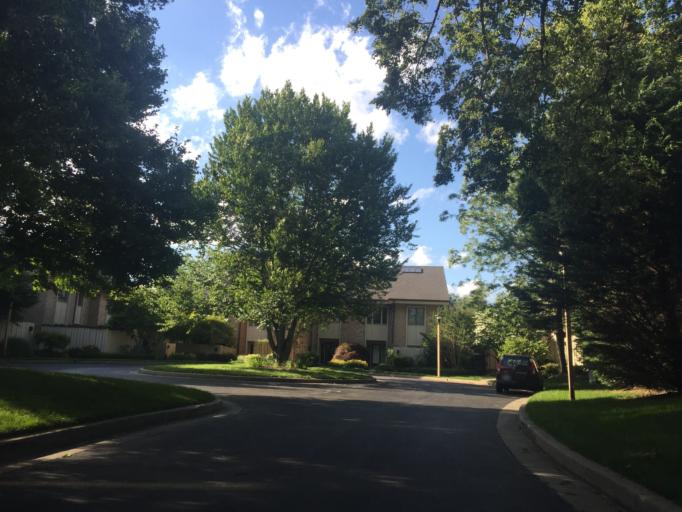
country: US
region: Maryland
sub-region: Baltimore County
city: Towson
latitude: 39.3672
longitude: -76.6365
